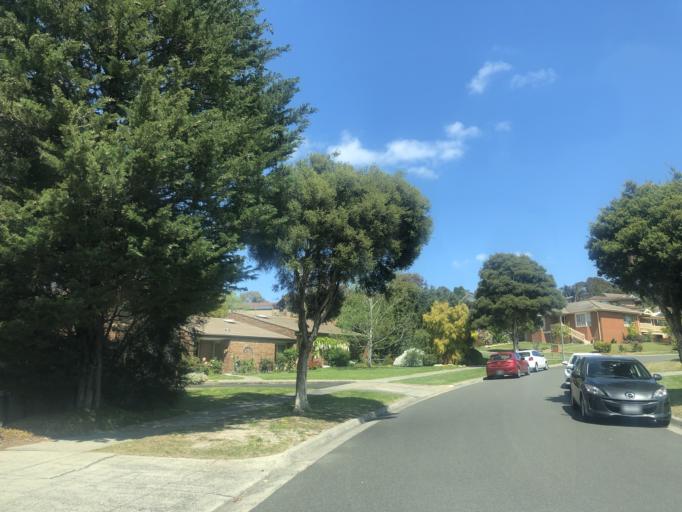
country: AU
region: Victoria
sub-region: Monash
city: Mulgrave
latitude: -37.9198
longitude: 145.1901
